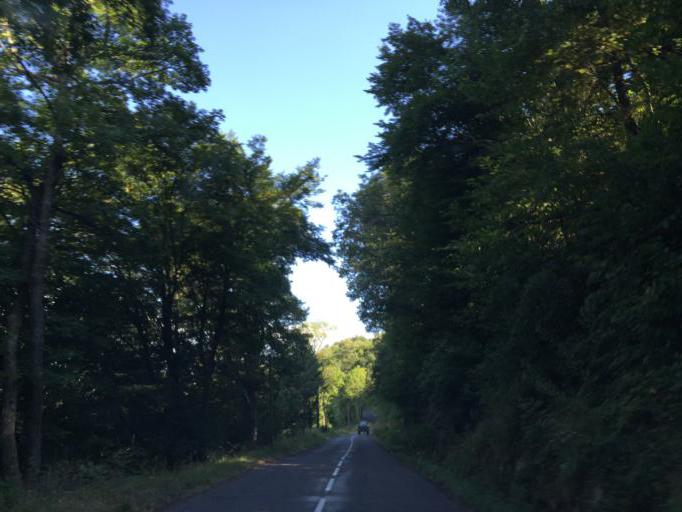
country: FR
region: Rhone-Alpes
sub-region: Departement de la Loire
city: Sorbiers
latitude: 45.5001
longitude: 4.4805
